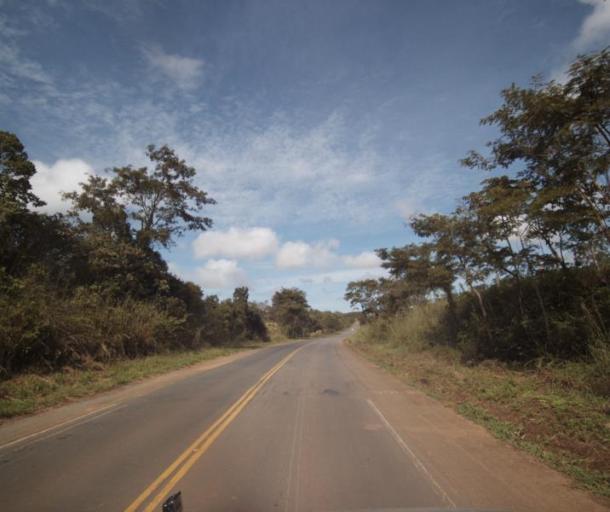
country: BR
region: Goias
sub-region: Pirenopolis
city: Pirenopolis
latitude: -15.9866
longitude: -48.8303
